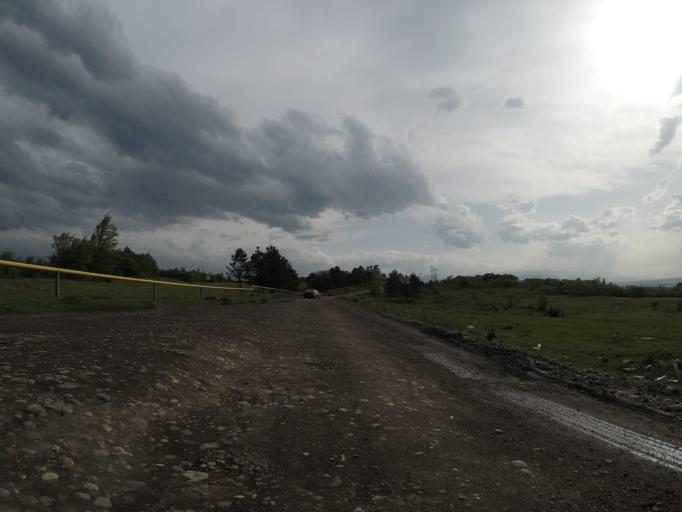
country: GE
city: Shorapani
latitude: 42.1788
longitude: 43.1350
